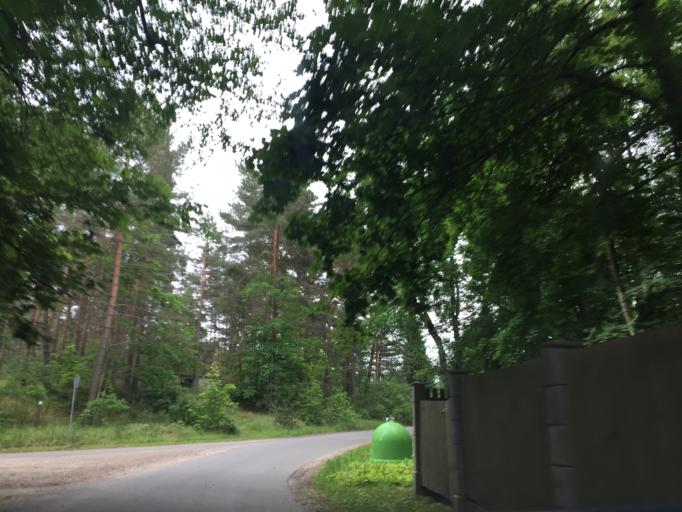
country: LV
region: Tukuma Rajons
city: Engure
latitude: 57.0801
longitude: 23.2691
